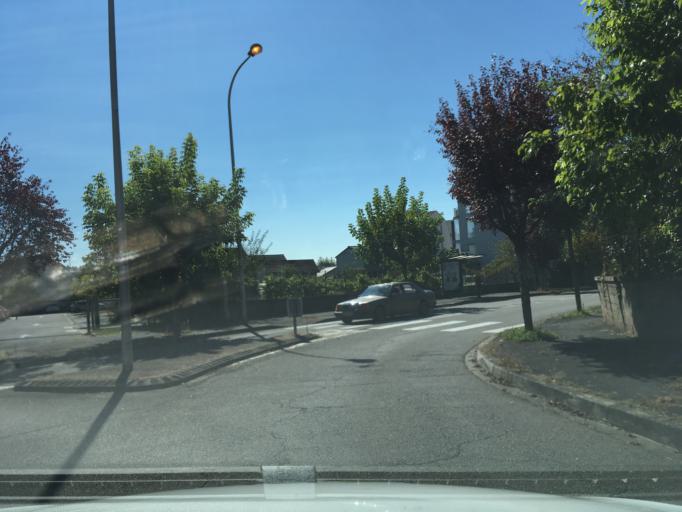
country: FR
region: Limousin
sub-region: Departement de la Correze
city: Brive-la-Gaillarde
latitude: 45.1678
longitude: 1.5280
